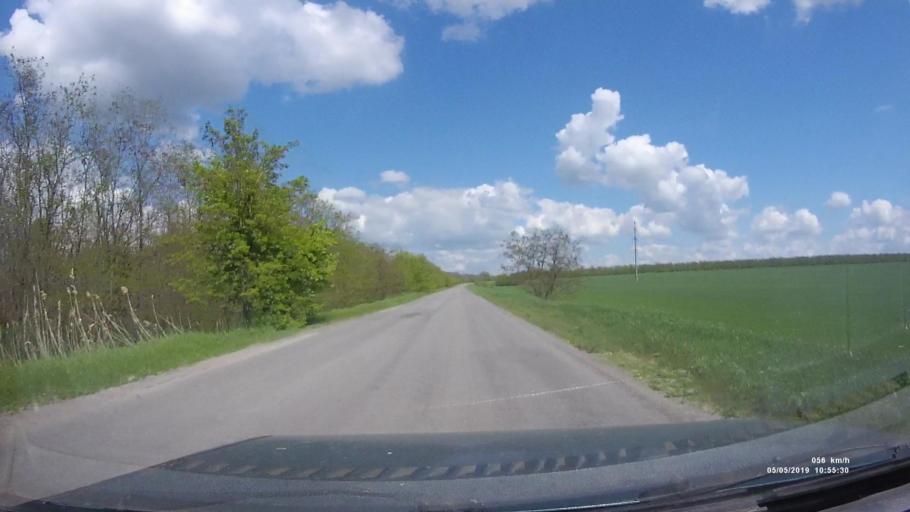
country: RU
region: Rostov
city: Ust'-Donetskiy
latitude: 47.6661
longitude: 40.8208
